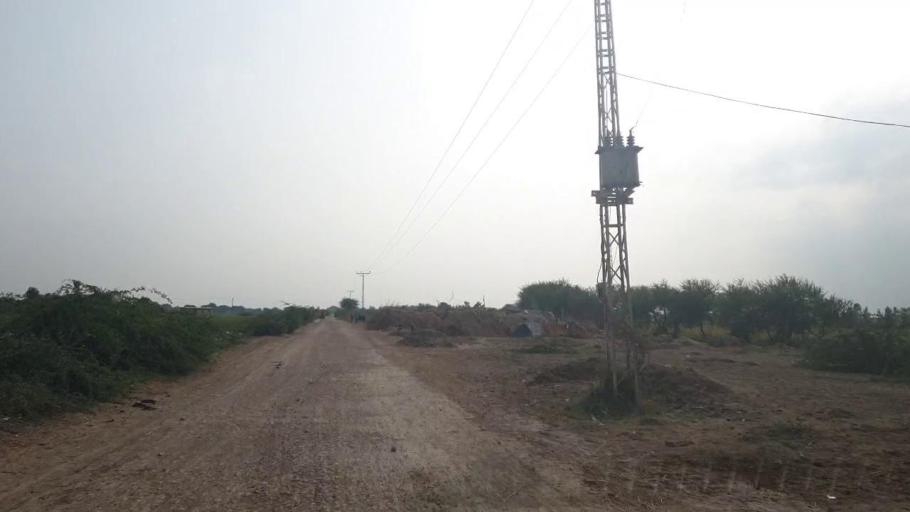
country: PK
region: Sindh
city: Badin
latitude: 24.6212
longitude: 68.6881
